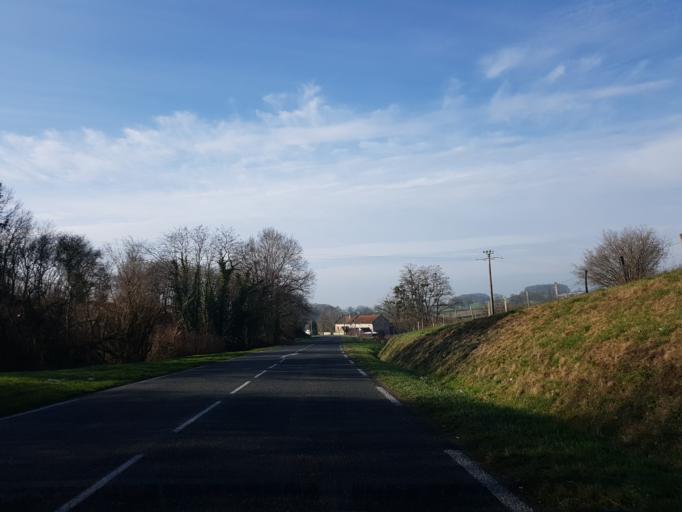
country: FR
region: Bourgogne
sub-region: Departement de Saone-et-Loire
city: La Motte-Saint-Jean
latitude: 46.5959
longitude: 3.9477
